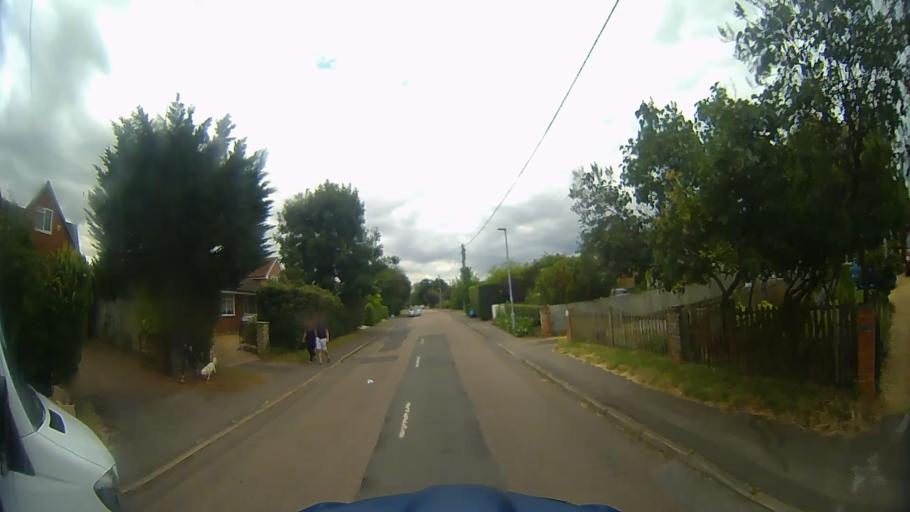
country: GB
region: England
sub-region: Wokingham
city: Winnersh
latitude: 51.4321
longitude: -0.8705
